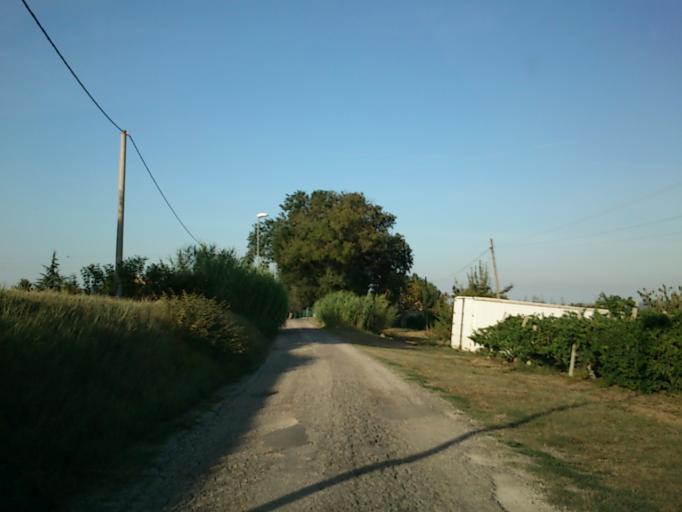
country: IT
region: The Marches
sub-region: Provincia di Pesaro e Urbino
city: Calcinelli
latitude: 43.7674
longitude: 12.9215
